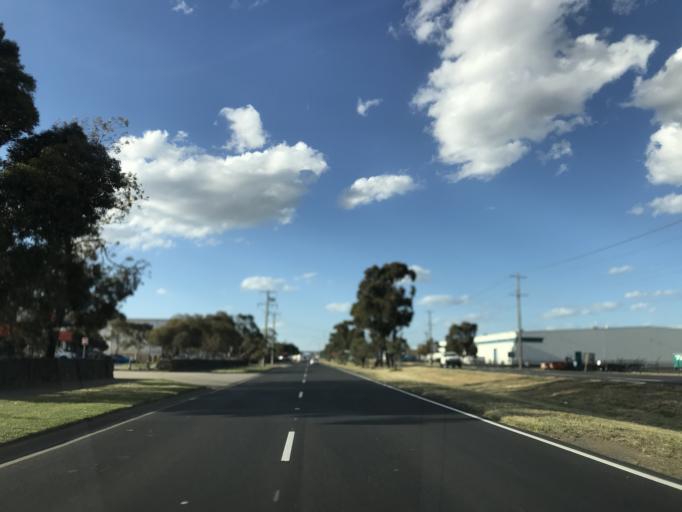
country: AU
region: Victoria
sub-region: Brimbank
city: Derrimut
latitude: -37.8170
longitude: 144.7868
